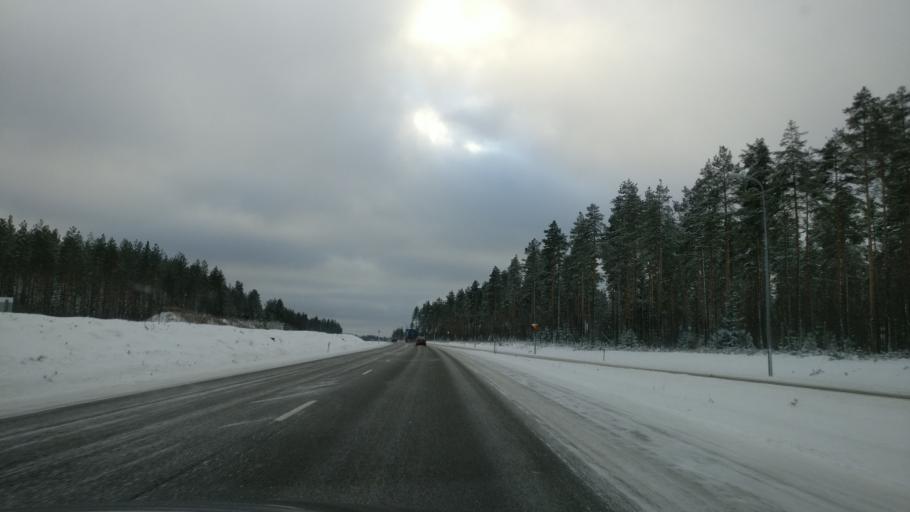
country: FI
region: Paijanne Tavastia
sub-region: Lahti
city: Heinola
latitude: 61.1116
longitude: 25.9209
